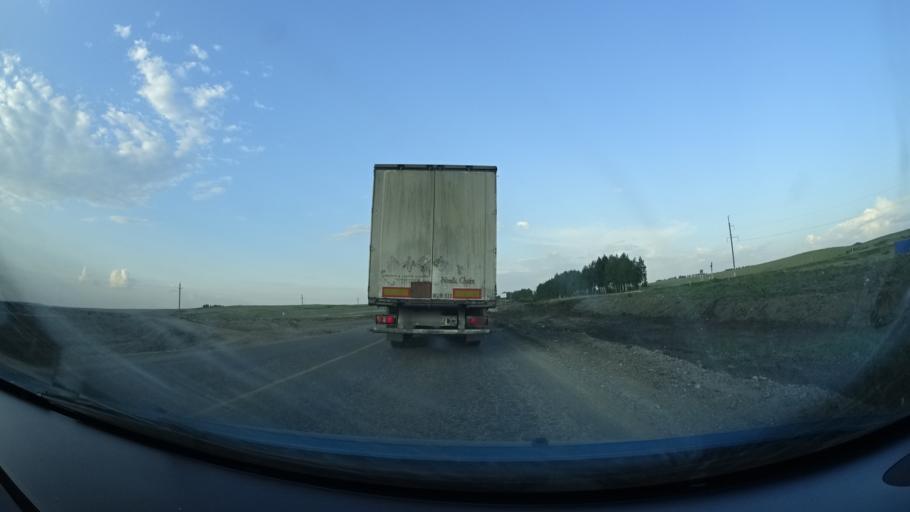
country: RU
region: Samara
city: Kamyshla
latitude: 54.0478
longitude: 52.0188
